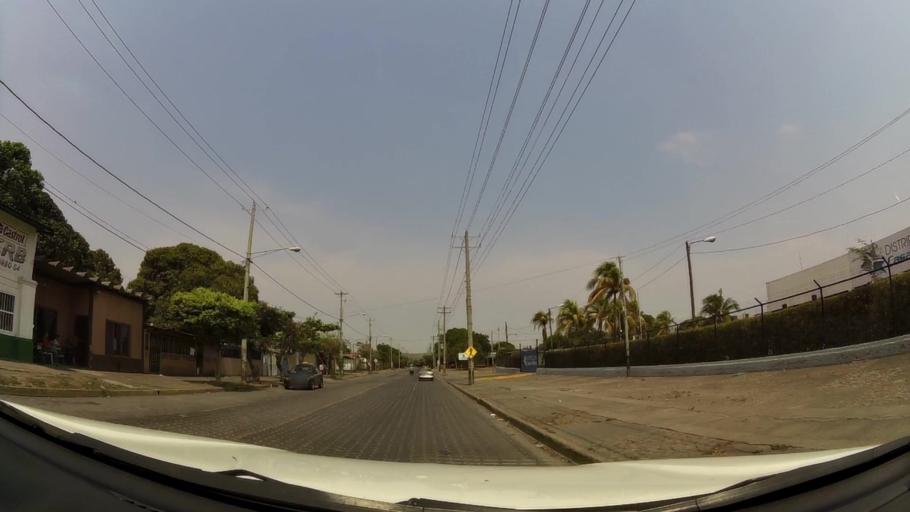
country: NI
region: Managua
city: Ciudad Sandino
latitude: 12.1581
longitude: -86.3008
